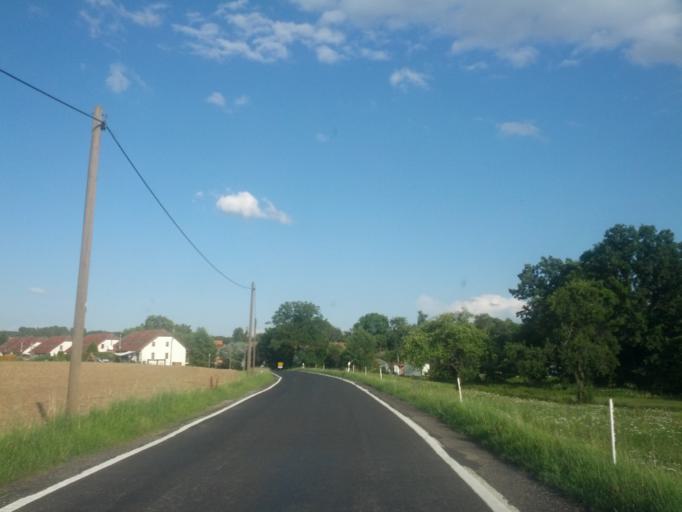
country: DE
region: Thuringia
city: Bischofroda
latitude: 51.0104
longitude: 10.3982
